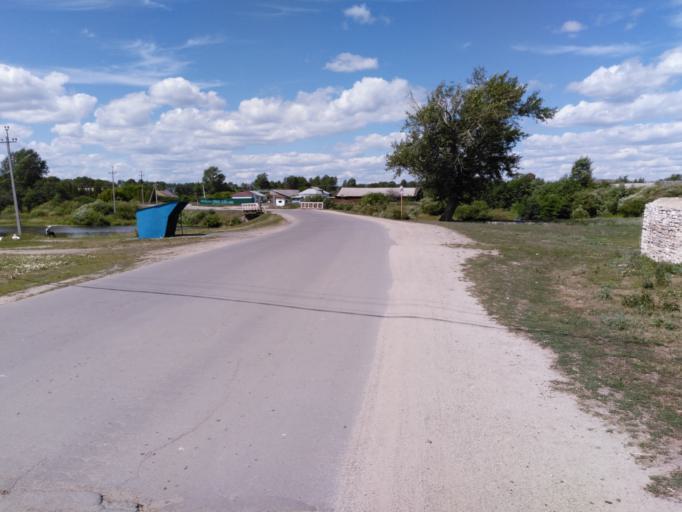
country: RU
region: Bashkortostan
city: Akhunovo
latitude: 54.2103
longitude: 59.6048
